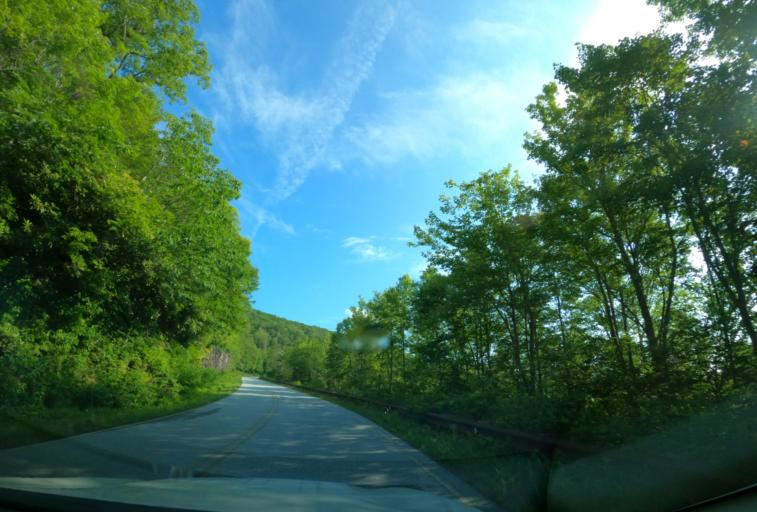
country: US
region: North Carolina
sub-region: Transylvania County
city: Brevard
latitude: 35.2744
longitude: -82.9173
